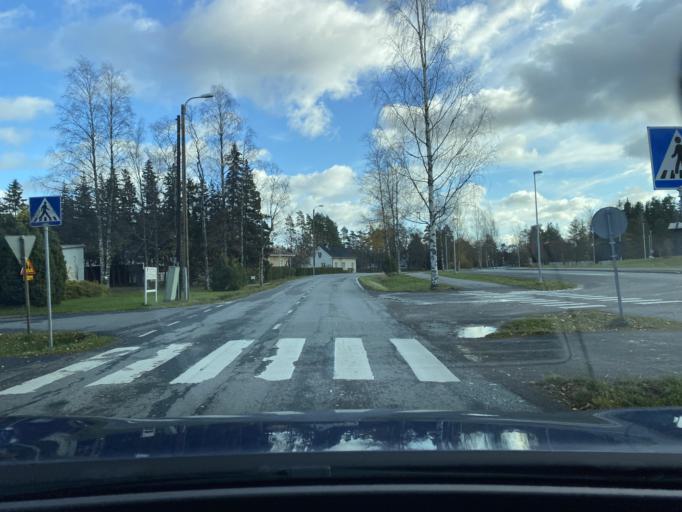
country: FI
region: Varsinais-Suomi
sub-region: Loimaa
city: Aura
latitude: 60.7221
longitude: 22.5979
